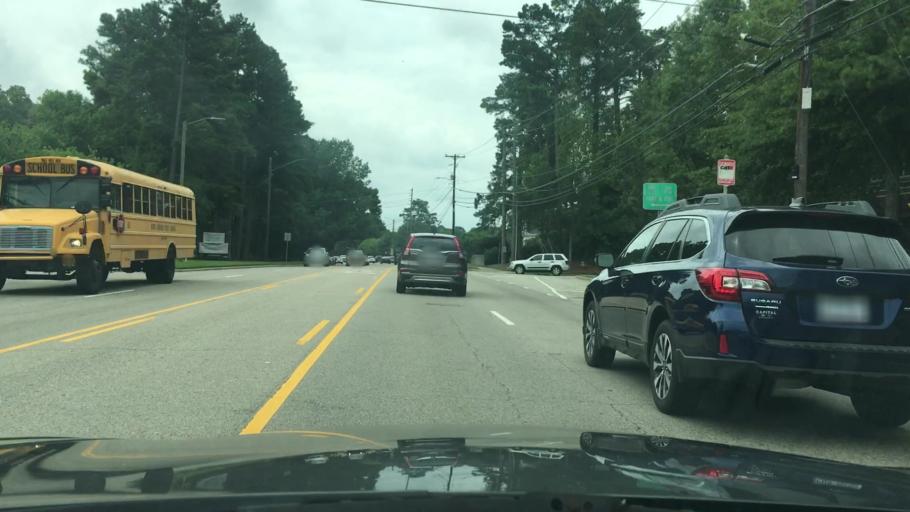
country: US
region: North Carolina
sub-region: Wake County
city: West Raleigh
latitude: 35.8502
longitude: -78.6437
